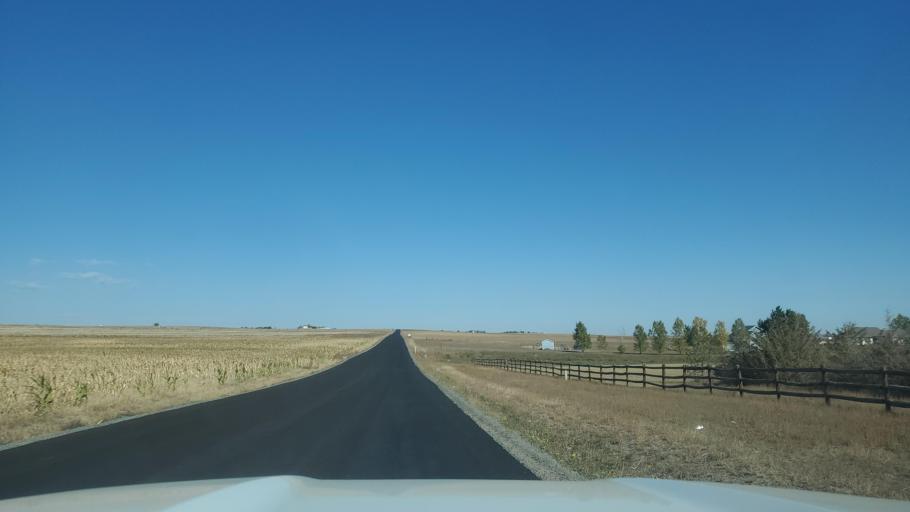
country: US
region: Colorado
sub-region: Adams County
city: Bennett
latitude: 39.7428
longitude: -104.3773
